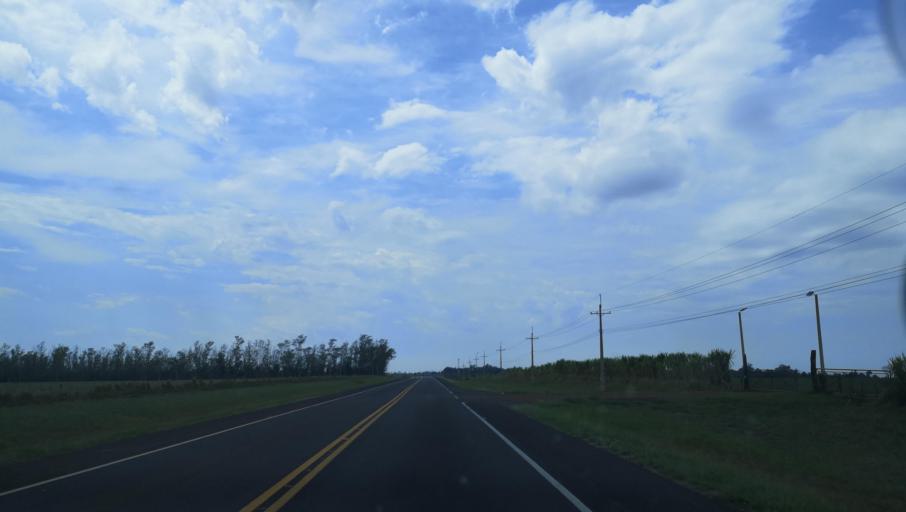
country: PY
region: Misiones
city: San Patricio
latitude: -26.9994
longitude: -56.7564
